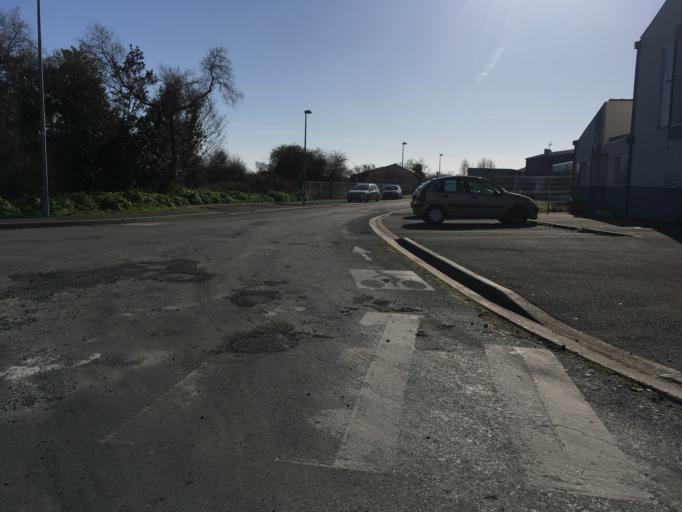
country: FR
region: Poitou-Charentes
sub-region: Departement de la Charente-Maritime
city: La Rochelle
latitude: 46.1500
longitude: -1.1432
